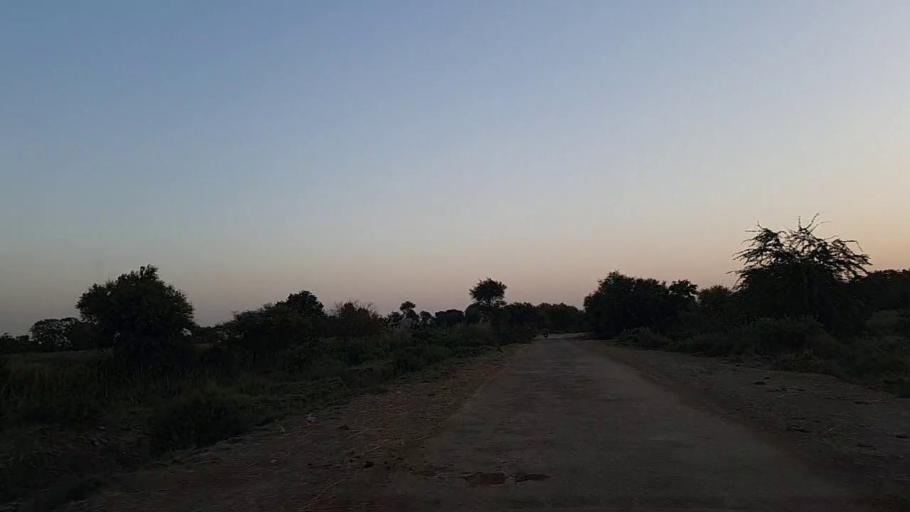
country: PK
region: Sindh
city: Mirpur Batoro
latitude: 24.6188
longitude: 68.1839
